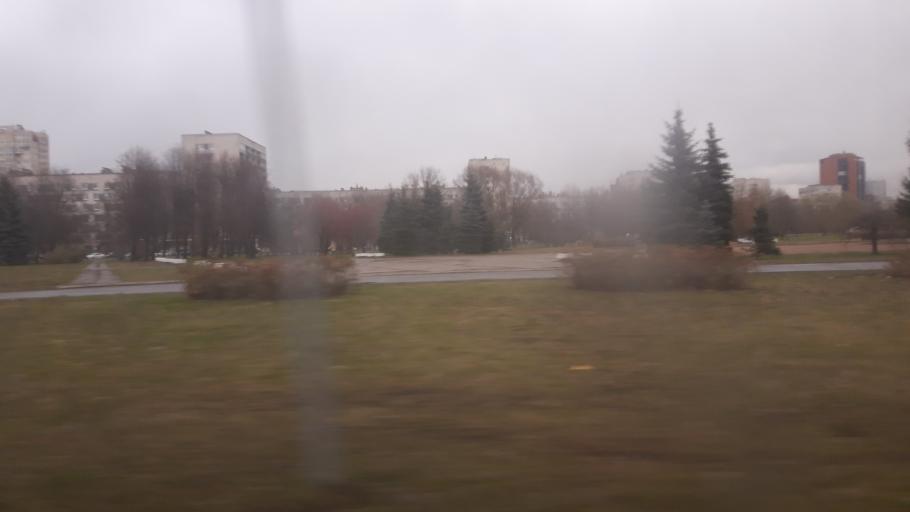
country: RU
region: St.-Petersburg
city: Kupchino
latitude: 59.8406
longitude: 30.3224
